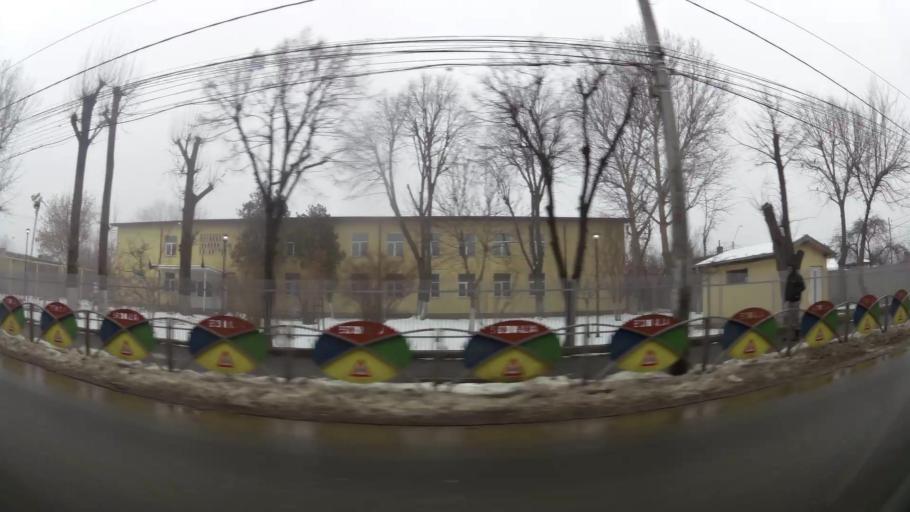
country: RO
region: Ilfov
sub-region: Comuna Chiajna
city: Rosu
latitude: 44.4723
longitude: 26.0183
